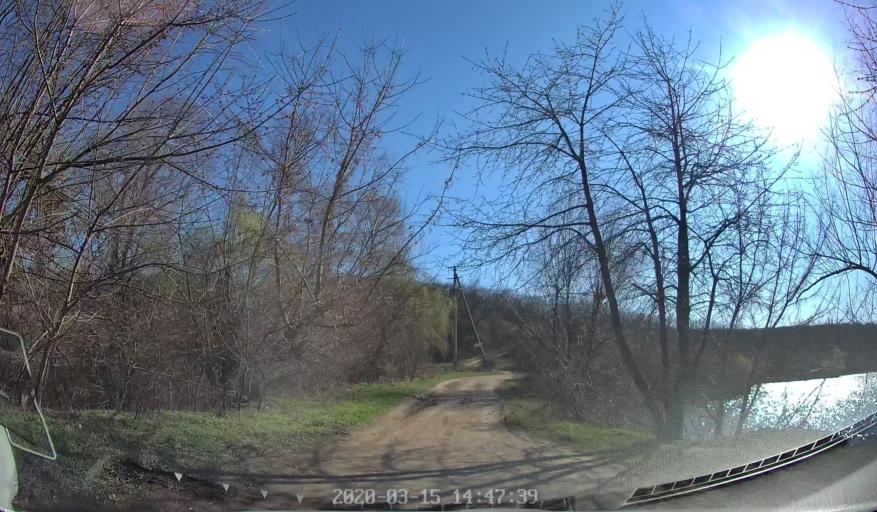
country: MD
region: Orhei
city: Orhei
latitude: 47.2816
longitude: 28.8325
